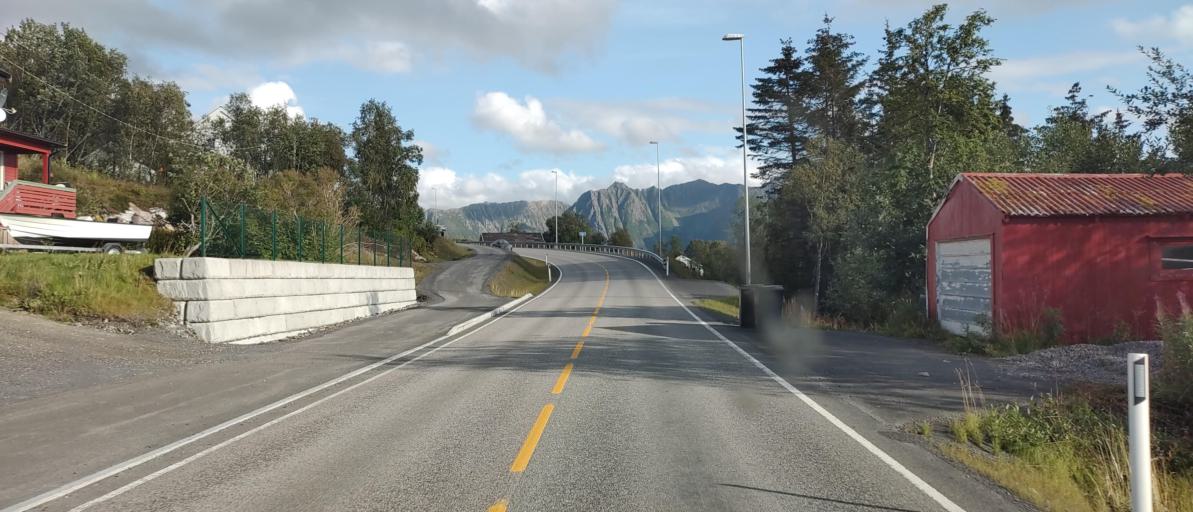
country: NO
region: Nordland
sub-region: Sortland
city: Sortland
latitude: 68.7522
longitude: 15.4741
